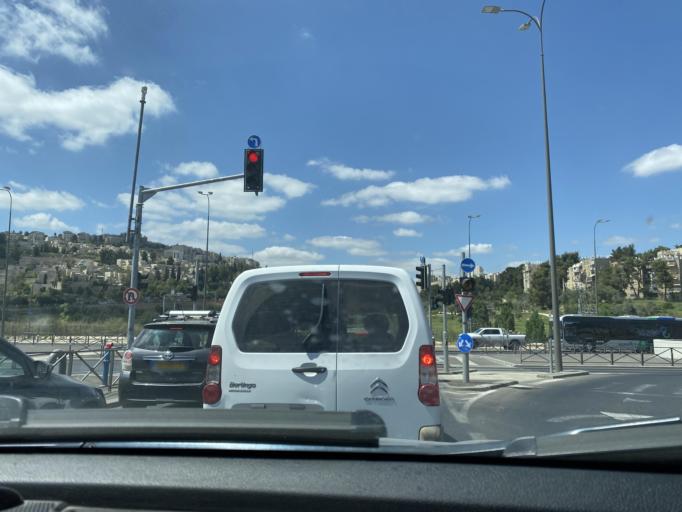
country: IL
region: Jerusalem
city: Jerusalem
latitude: 31.7573
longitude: 35.1978
